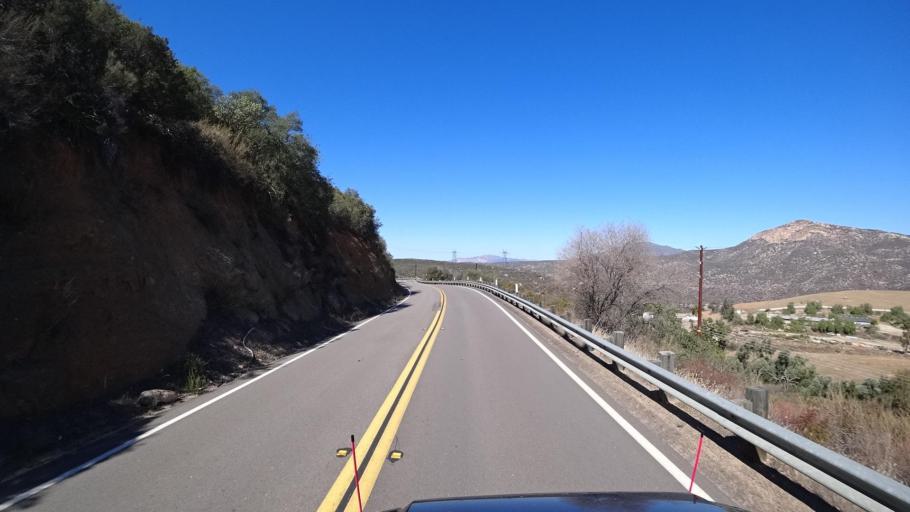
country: US
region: California
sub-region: San Diego County
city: Alpine
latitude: 32.7744
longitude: -116.7082
